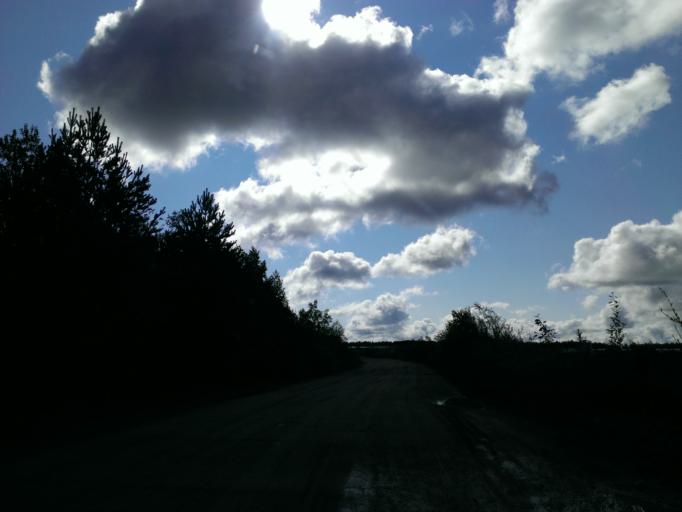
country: LV
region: Incukalns
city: Vangazi
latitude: 57.0920
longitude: 24.5067
